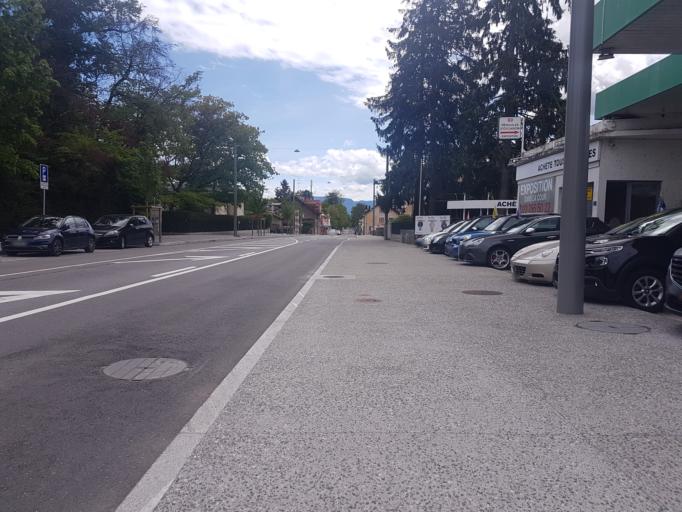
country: CH
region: Geneva
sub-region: Geneva
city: Versoix
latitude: 46.2908
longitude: 6.1657
